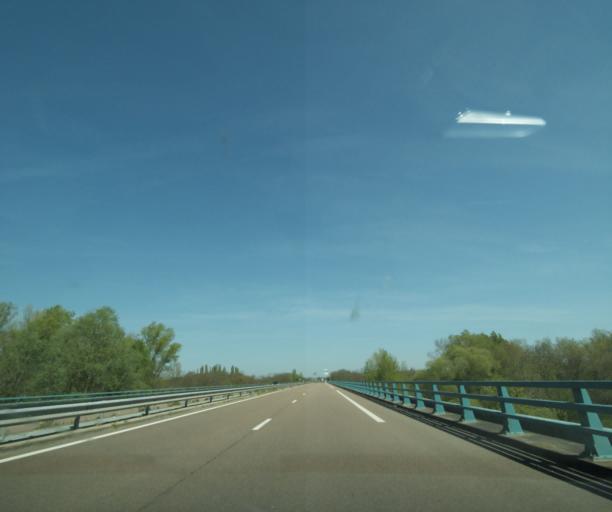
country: FR
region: Bourgogne
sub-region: Departement de la Nievre
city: Saint-Eloi
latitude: 46.9736
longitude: 3.1963
